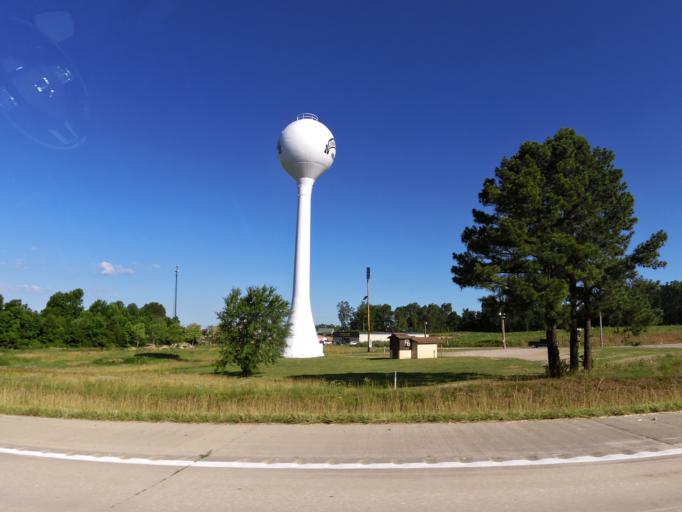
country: US
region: Missouri
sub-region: Butler County
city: Poplar Bluff
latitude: 36.6633
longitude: -90.5160
